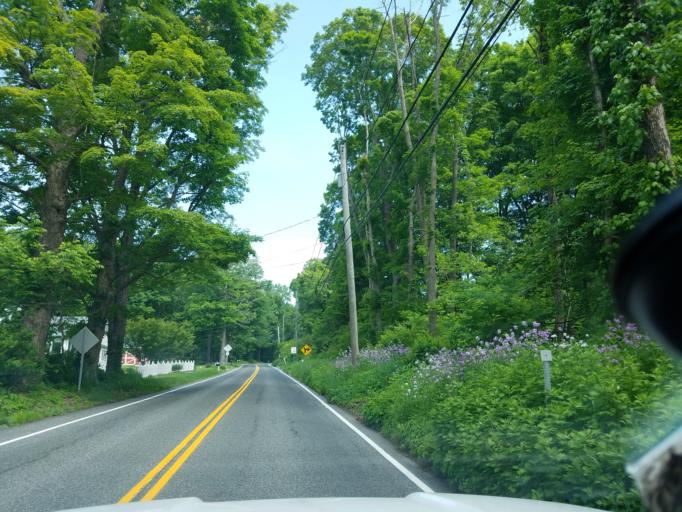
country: US
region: Connecticut
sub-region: Fairfield County
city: Sherman
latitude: 41.5422
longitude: -73.4984
